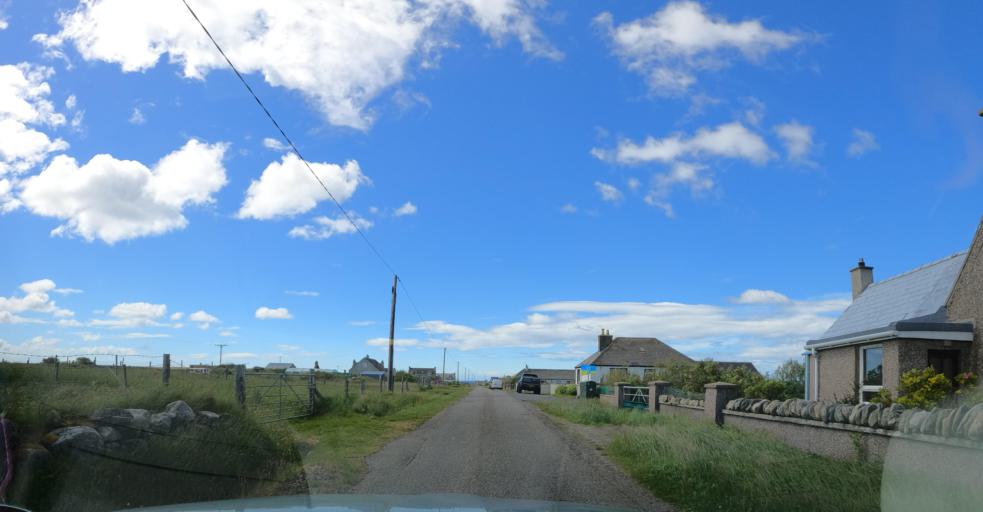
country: GB
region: Scotland
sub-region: Eilean Siar
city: Isle of Lewis
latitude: 58.3574
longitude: -6.5571
